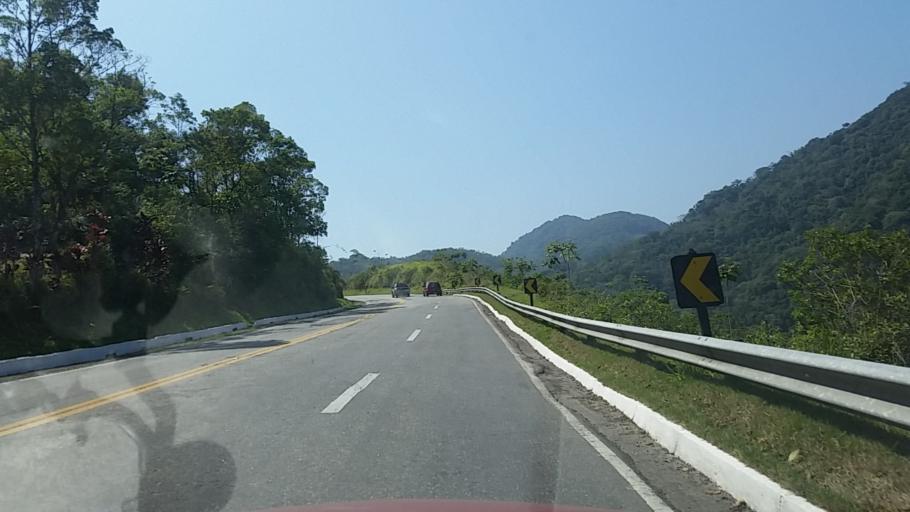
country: BR
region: Sao Paulo
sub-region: Miracatu
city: Miracatu
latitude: -24.3801
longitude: -47.5021
